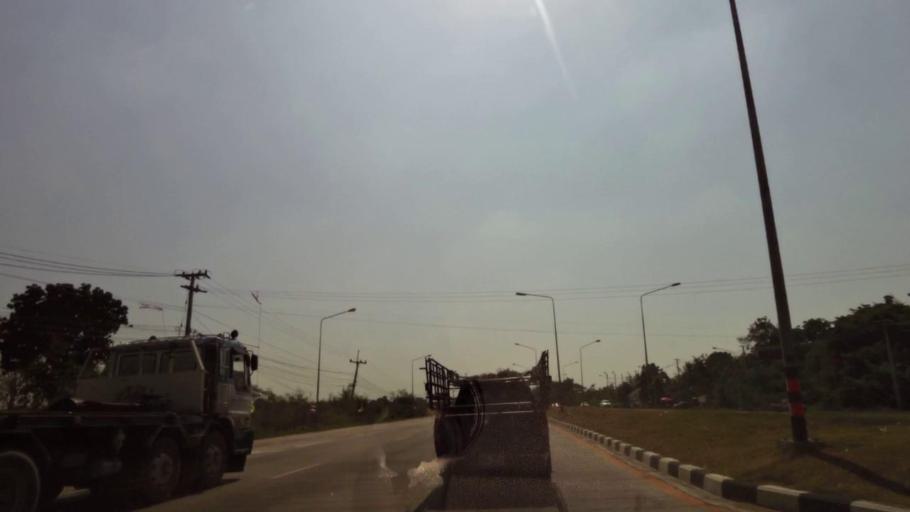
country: TH
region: Phichit
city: Wachira Barami
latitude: 16.3548
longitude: 100.1290
